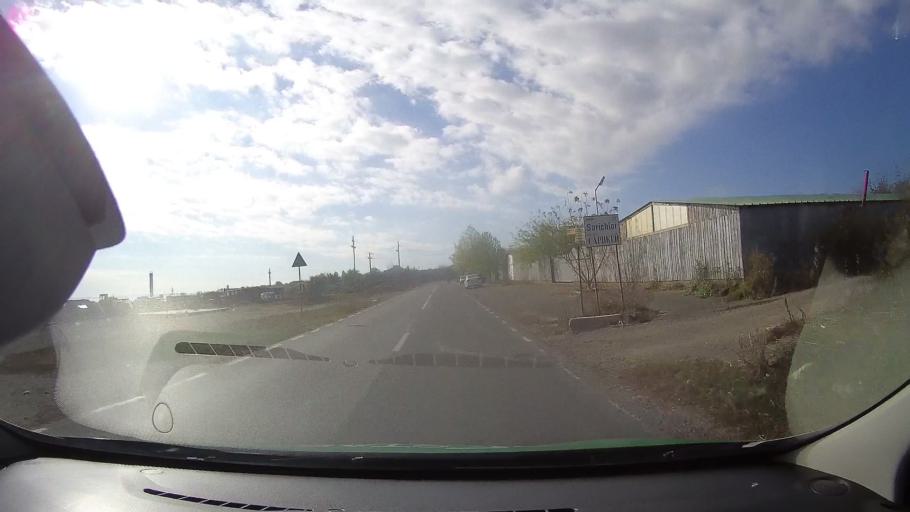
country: RO
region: Tulcea
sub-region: Comuna Sarichioi
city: Sarichioi
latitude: 44.9576
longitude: 28.8571
